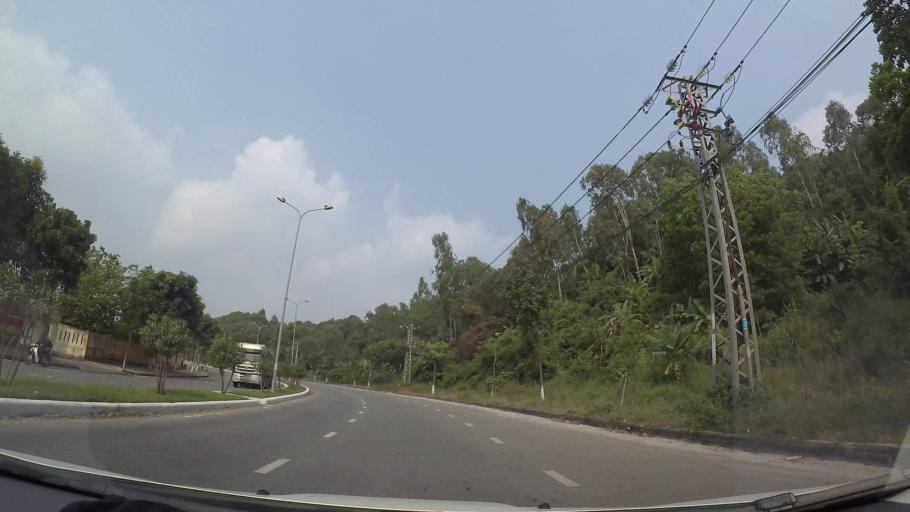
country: VN
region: Da Nang
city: Da Nang
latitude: 16.1181
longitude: 108.2293
